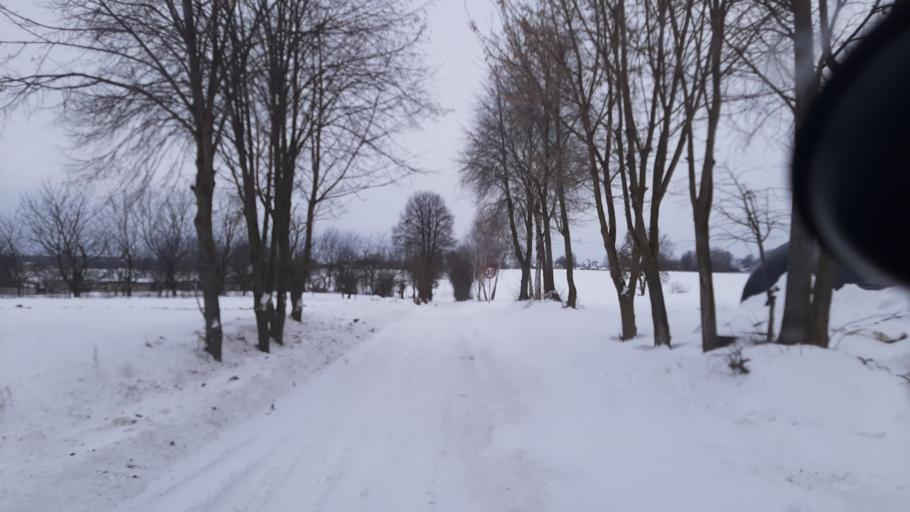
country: PL
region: Lublin Voivodeship
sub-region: Powiat lubelski
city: Garbow
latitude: 51.3303
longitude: 22.2981
